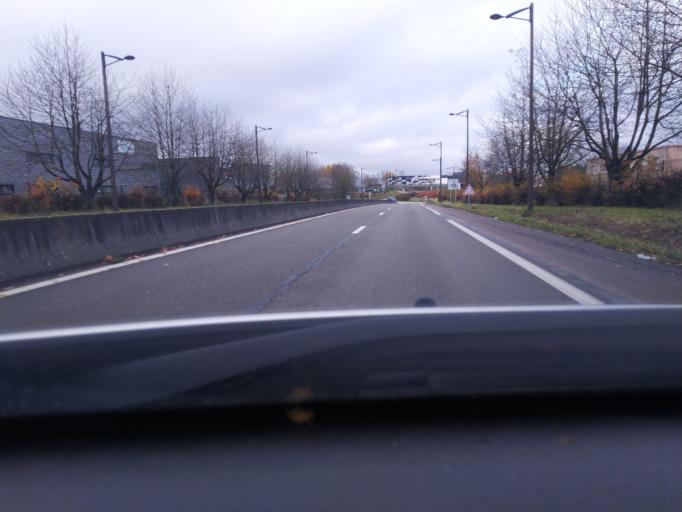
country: FR
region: Haute-Normandie
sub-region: Departement de la Seine-Maritime
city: Maromme
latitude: 49.4869
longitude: 1.0163
